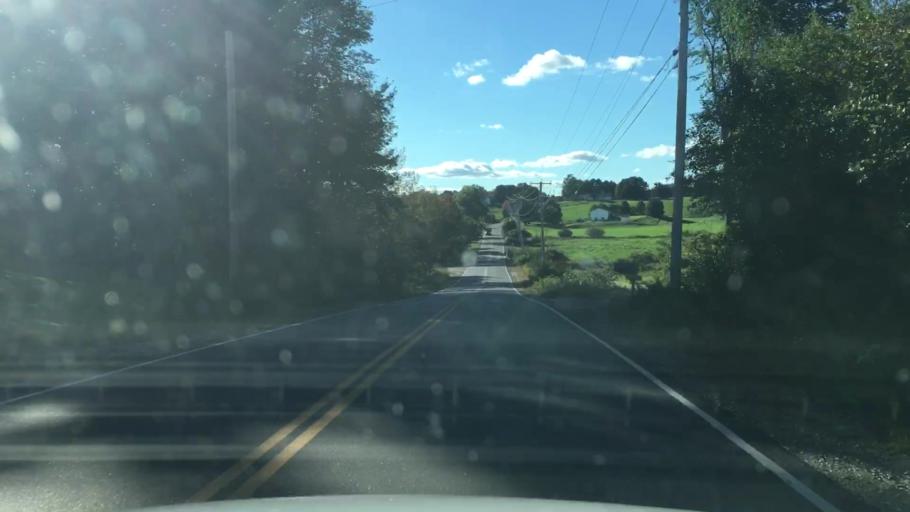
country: US
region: Maine
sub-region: Androscoggin County
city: Lisbon
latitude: 44.0748
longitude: -70.1019
